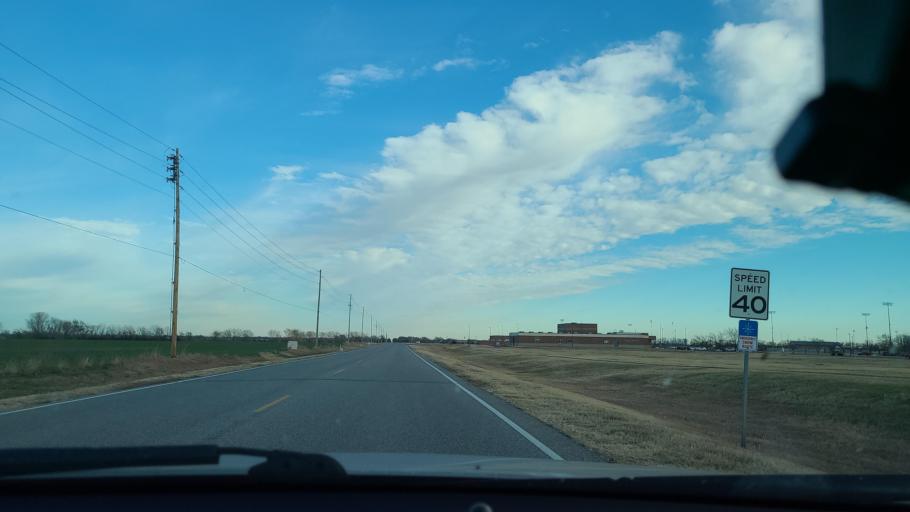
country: US
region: Kansas
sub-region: Sedgwick County
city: Goddard
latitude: 37.6496
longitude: -97.5706
